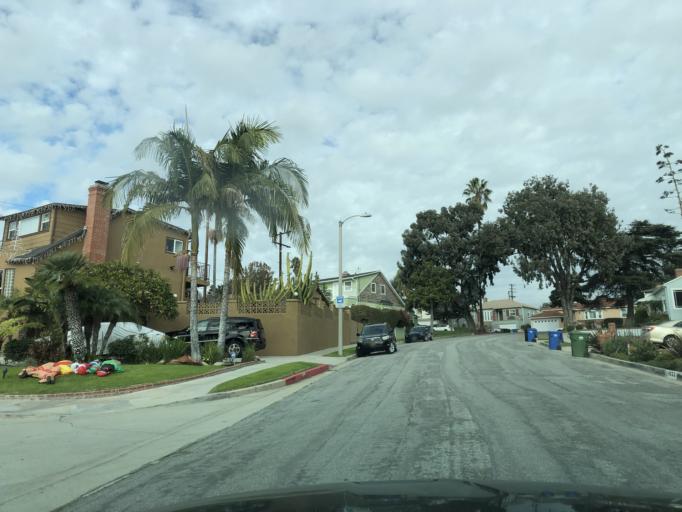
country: US
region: California
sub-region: Los Angeles County
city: View Park-Windsor Hills
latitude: 33.9937
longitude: -118.3569
